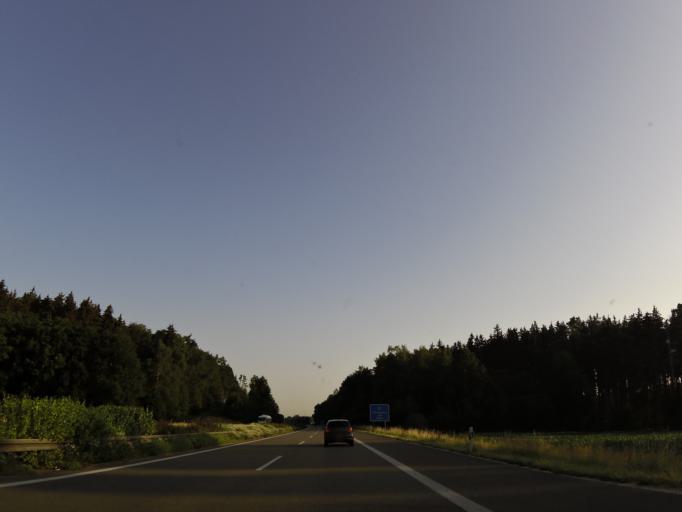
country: DE
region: Bavaria
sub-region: Swabia
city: Illertissen
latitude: 48.2341
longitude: 10.1235
